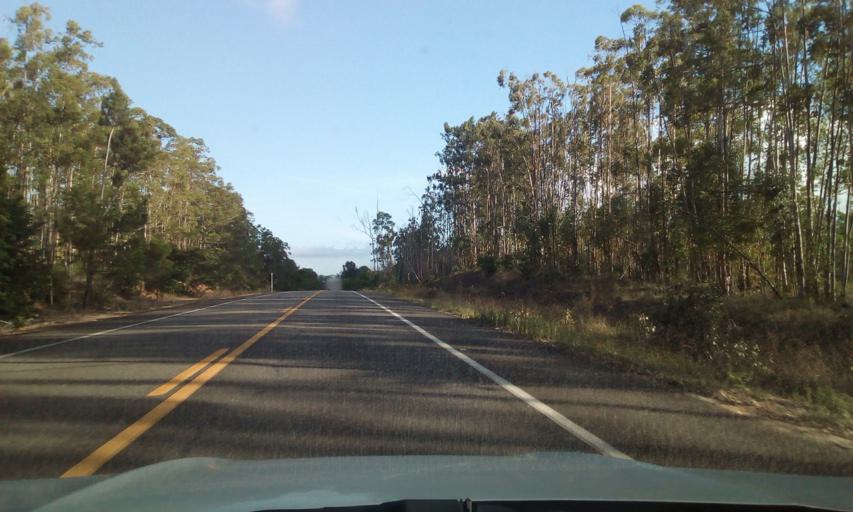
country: BR
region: Bahia
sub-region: Entre Rios
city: Entre Rios
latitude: -12.3192
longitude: -37.9044
